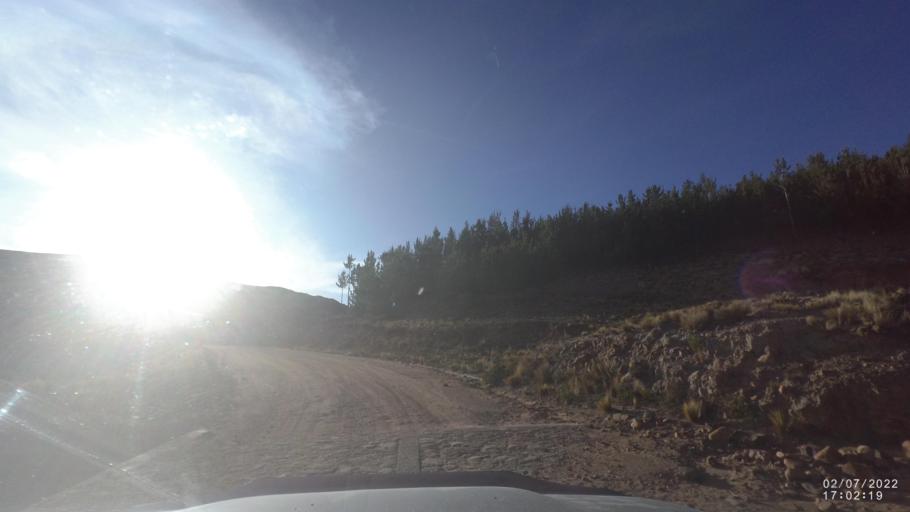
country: BO
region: Cochabamba
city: Irpa Irpa
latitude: -17.9264
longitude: -66.5541
